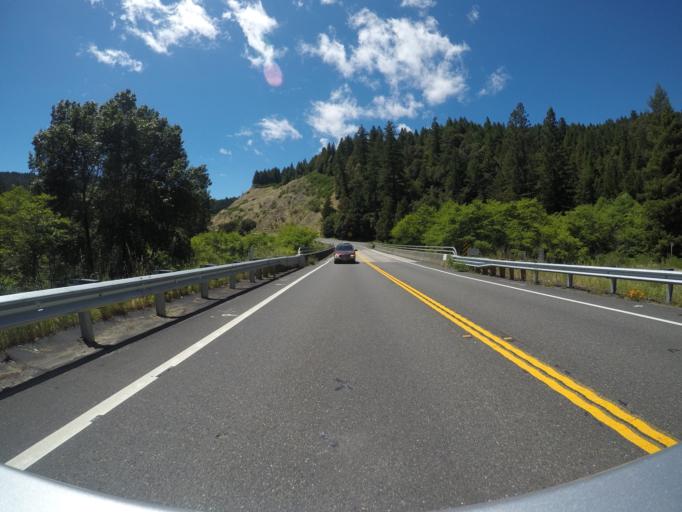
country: US
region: California
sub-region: Humboldt County
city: Redway
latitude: 39.9069
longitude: -123.7528
